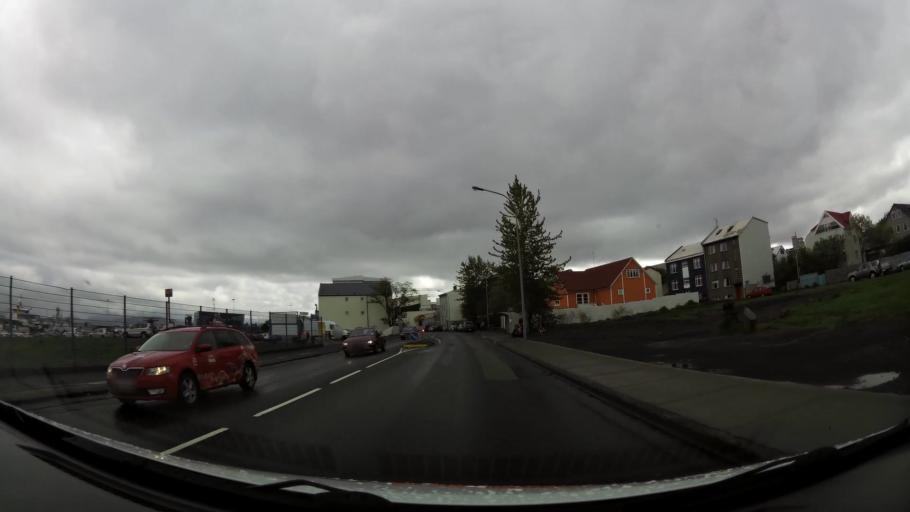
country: IS
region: Capital Region
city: Seltjarnarnes
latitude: 64.1517
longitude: -21.9494
